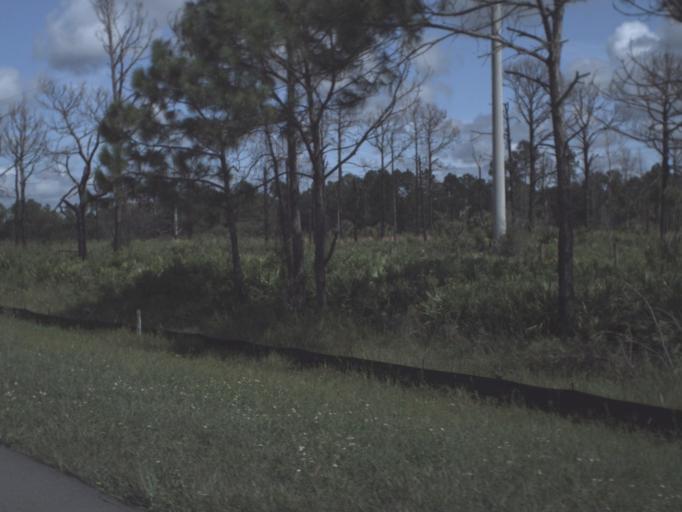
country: US
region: Florida
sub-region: Charlotte County
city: Port Charlotte
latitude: 27.0721
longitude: -82.0983
